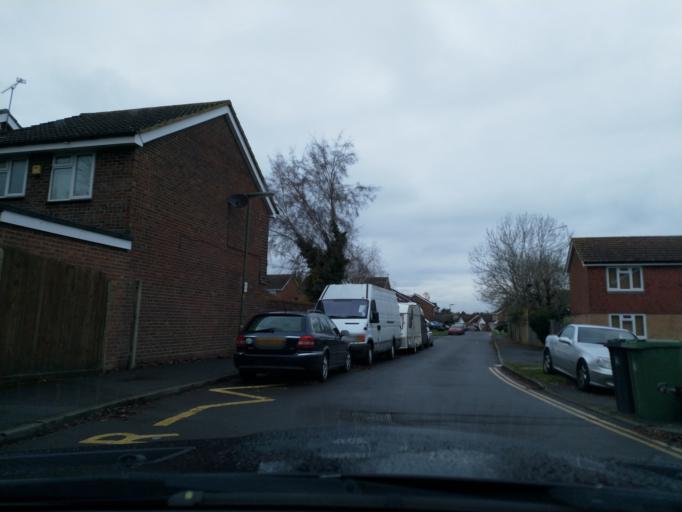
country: GB
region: England
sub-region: Surrey
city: Frimley
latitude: 51.3091
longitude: -0.7265
